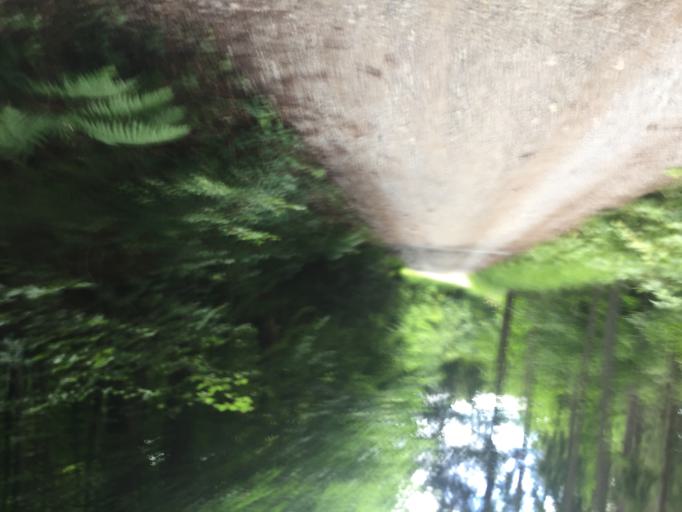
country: CH
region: Bern
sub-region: Thun District
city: Wattenwil
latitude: 46.7591
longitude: 7.4795
